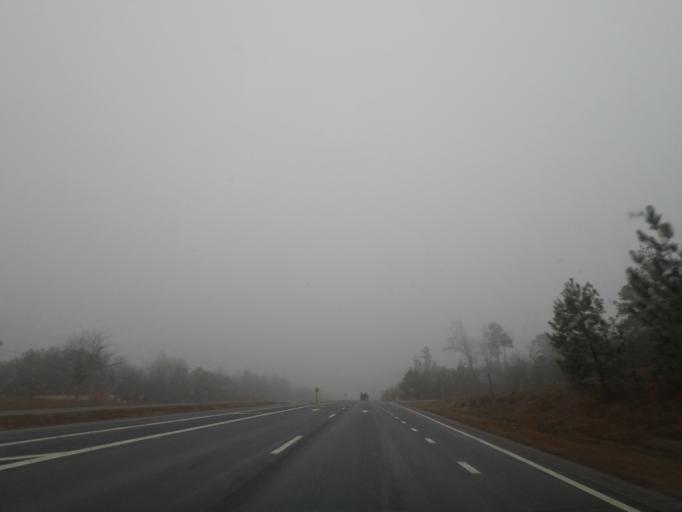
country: US
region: North Carolina
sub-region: Lee County
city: Sanford
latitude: 35.3853
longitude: -79.2312
